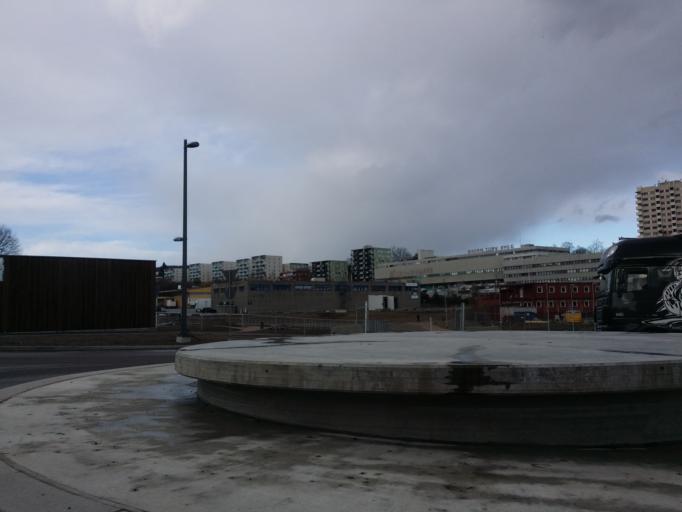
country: NO
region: Oslo
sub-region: Oslo
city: Oslo
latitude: 59.9305
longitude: 10.8027
